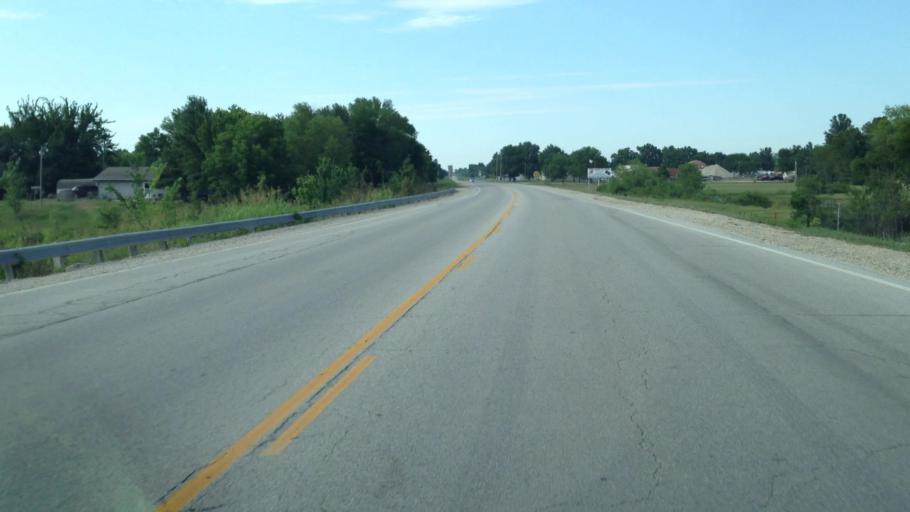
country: US
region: Kansas
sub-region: Neosho County
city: Erie
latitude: 37.5655
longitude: -95.2527
